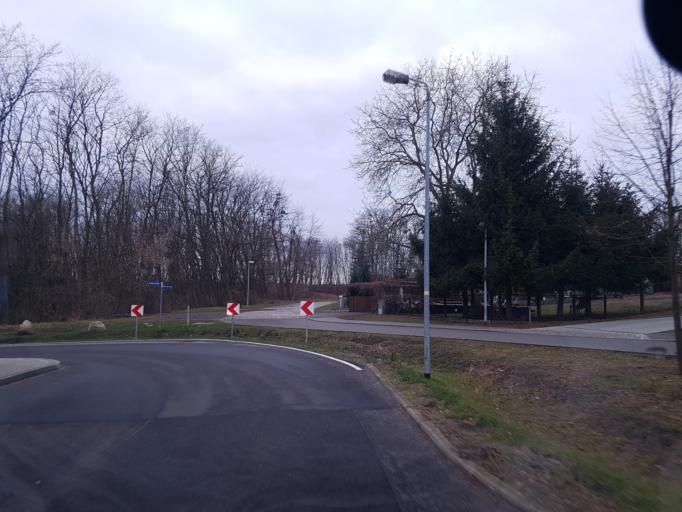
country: DE
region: Brandenburg
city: Senftenberg
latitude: 51.5293
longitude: 13.9471
